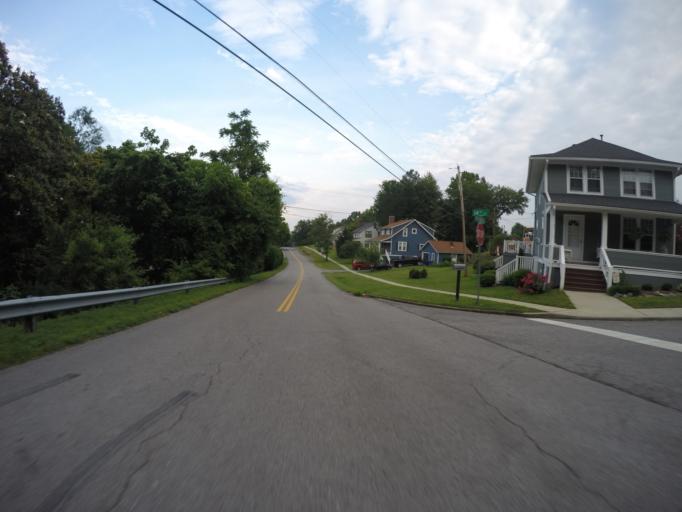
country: US
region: Tennessee
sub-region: Davidson County
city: Lakewood
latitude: 36.2564
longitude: -86.6426
